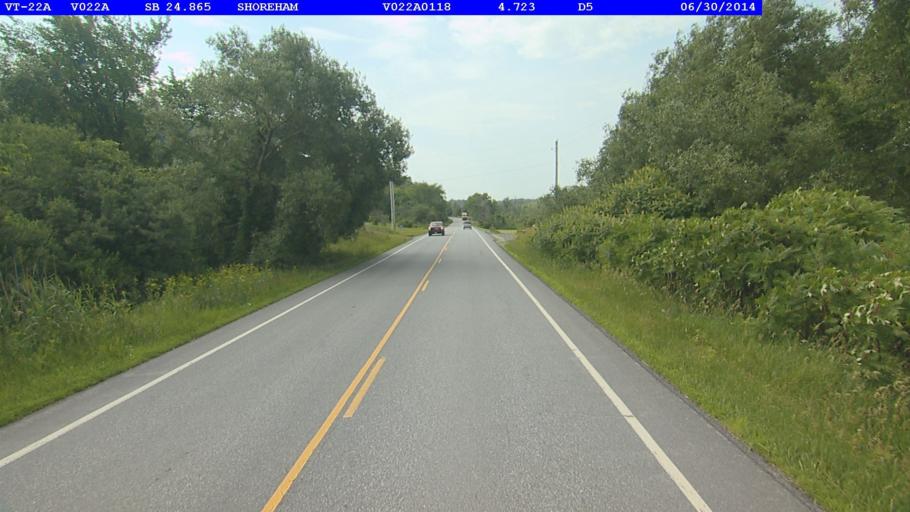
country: US
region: New York
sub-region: Essex County
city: Ticonderoga
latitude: 43.9172
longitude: -73.3124
